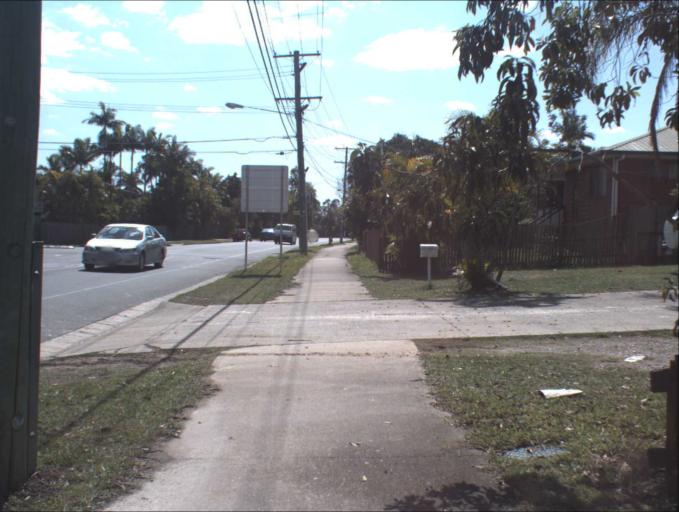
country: AU
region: Queensland
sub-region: Logan
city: Waterford West
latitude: -27.6744
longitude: 153.1116
